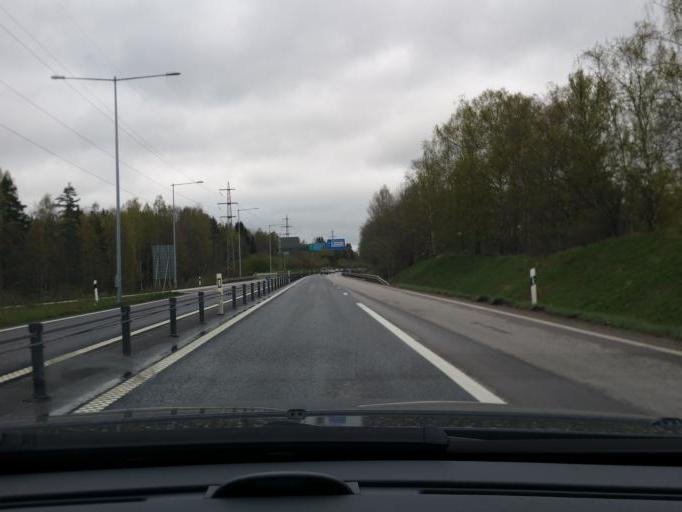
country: SE
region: Kronoberg
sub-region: Vaxjo Kommun
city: Vaexjoe
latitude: 56.8961
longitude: 14.7787
